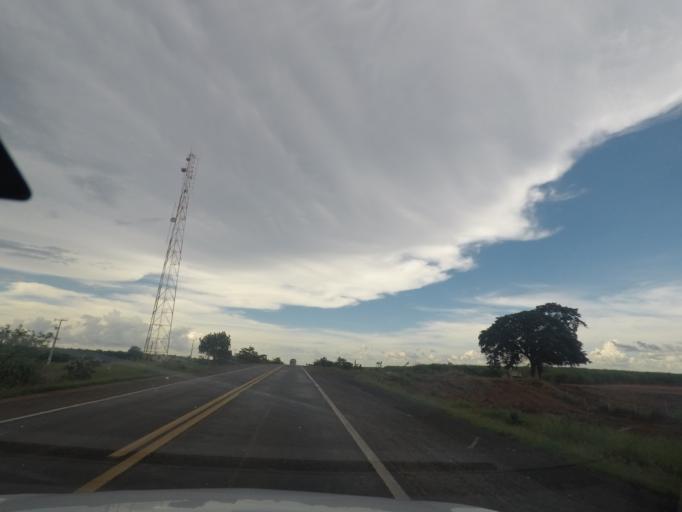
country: BR
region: Minas Gerais
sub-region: Prata
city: Prata
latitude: -19.5994
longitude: -48.8338
